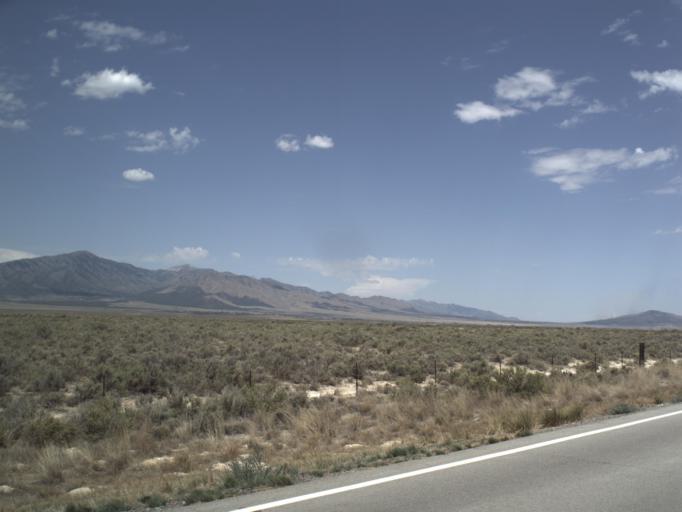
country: US
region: Utah
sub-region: Tooele County
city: Tooele
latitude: 40.2498
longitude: -112.3996
